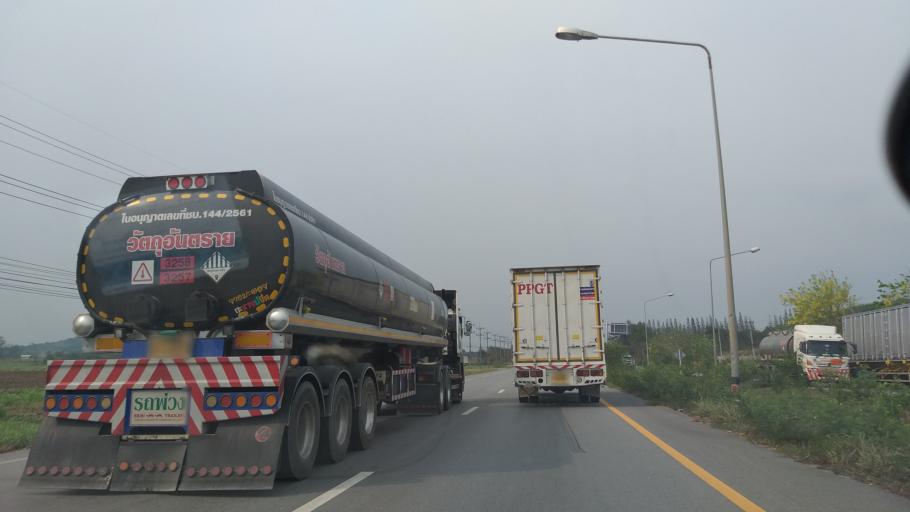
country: TH
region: Chon Buri
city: Ban Bueng
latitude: 13.2552
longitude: 101.2466
